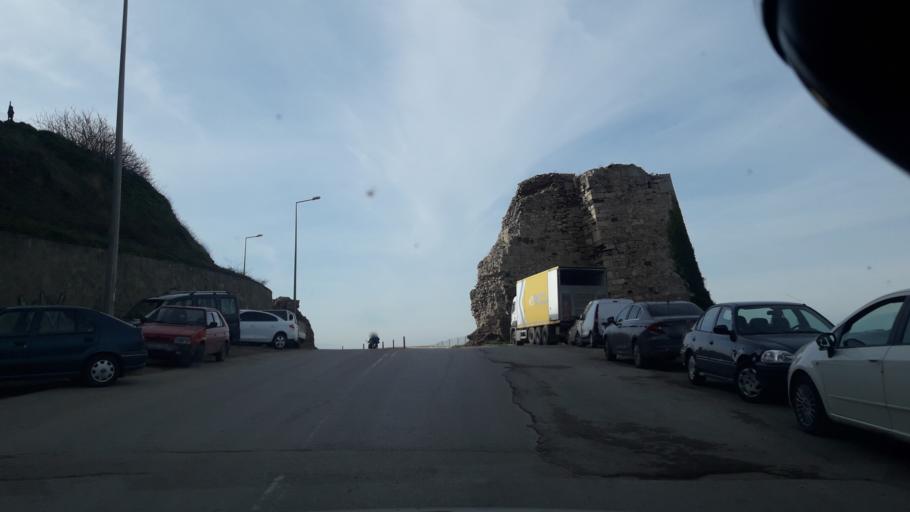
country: TR
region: Sinop
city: Sinop
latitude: 42.0261
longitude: 35.1417
